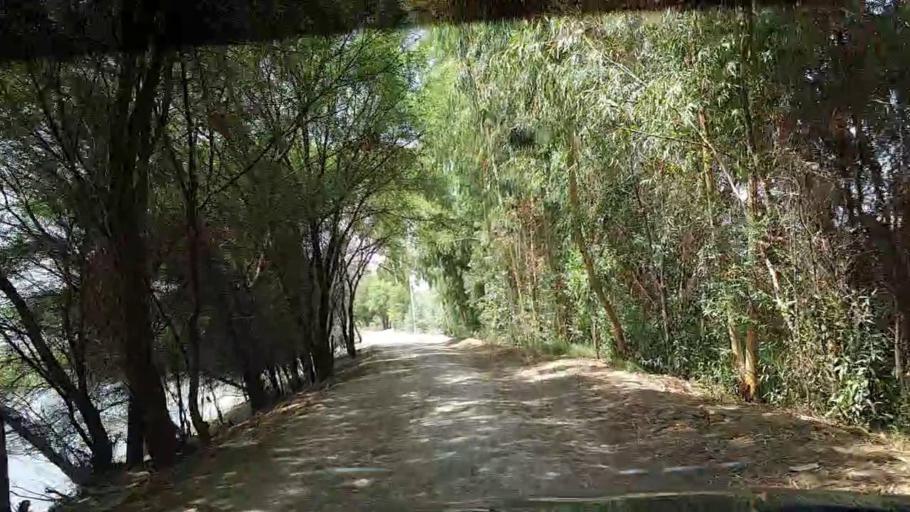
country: PK
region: Sindh
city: Ghotki
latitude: 28.0952
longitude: 69.3128
